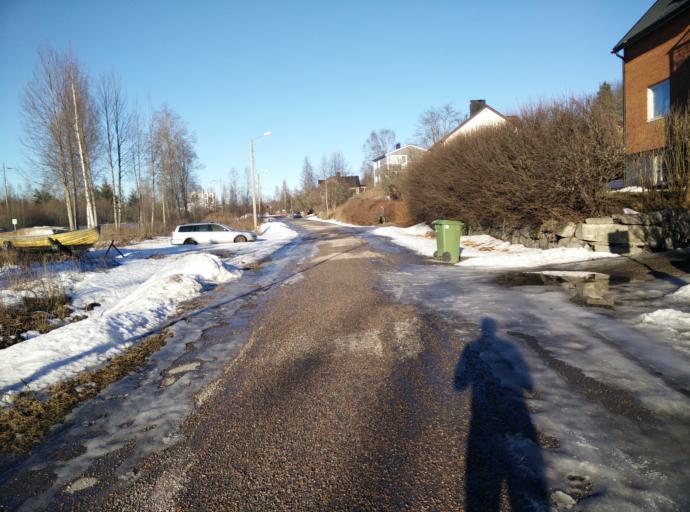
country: SE
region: Vaesternorrland
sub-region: Sundsvalls Kommun
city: Skottsund
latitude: 62.3042
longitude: 17.3848
